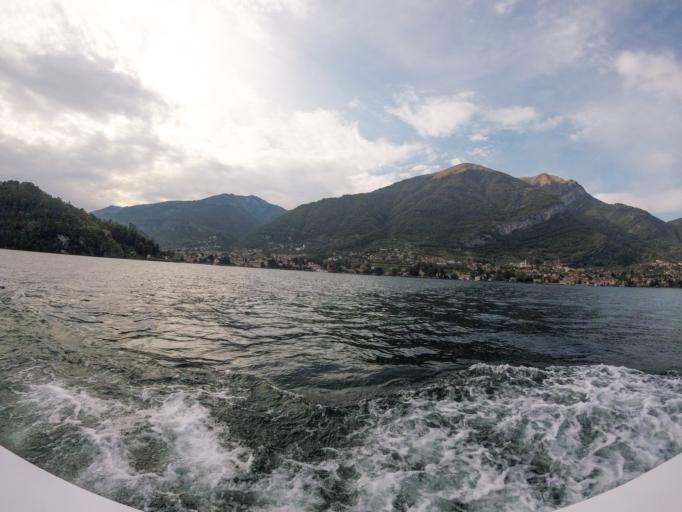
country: IT
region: Lombardy
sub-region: Provincia di Como
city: Mezzegra
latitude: 45.9699
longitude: 9.2096
